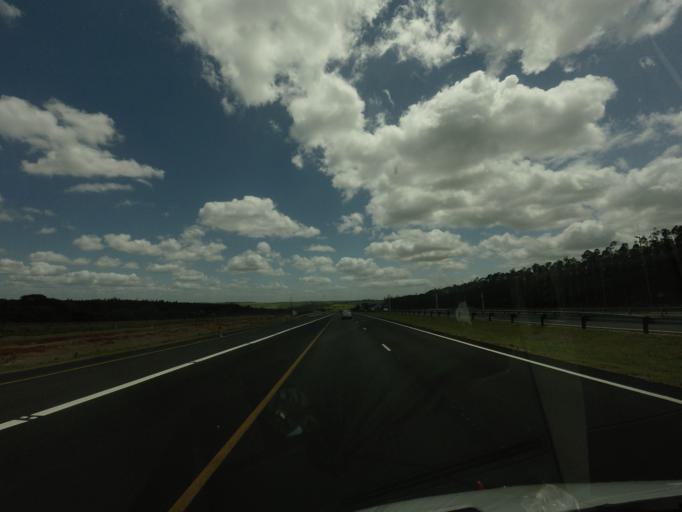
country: ZA
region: KwaZulu-Natal
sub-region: uThungulu District Municipality
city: KwaMbonambi
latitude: -28.5136
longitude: 32.1377
